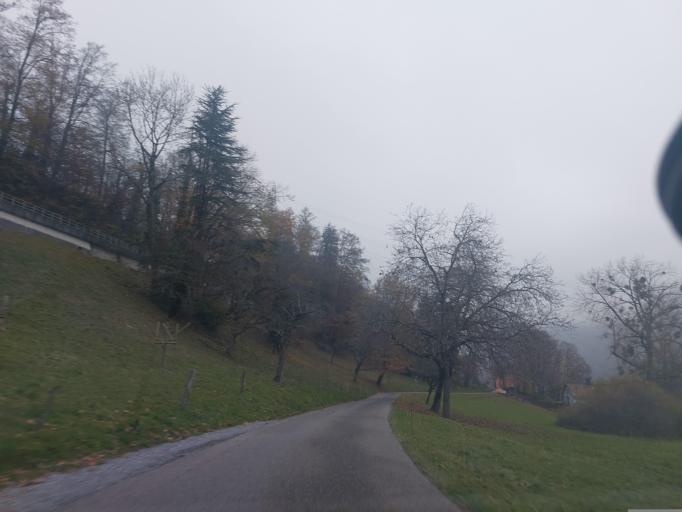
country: CH
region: Fribourg
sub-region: Veveyse District
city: Attalens
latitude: 46.4956
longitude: 6.8726
